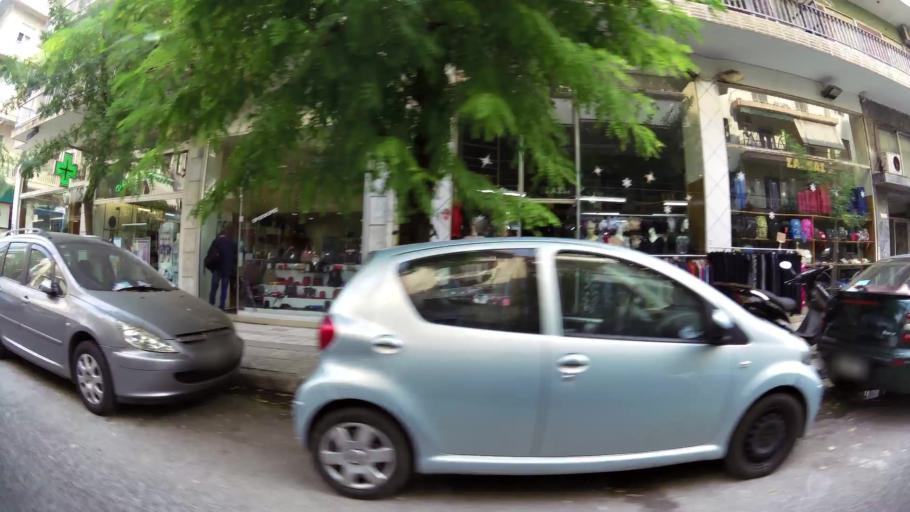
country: GR
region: Attica
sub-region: Nomarchia Athinas
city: Kipseli
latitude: 37.9981
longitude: 23.7409
